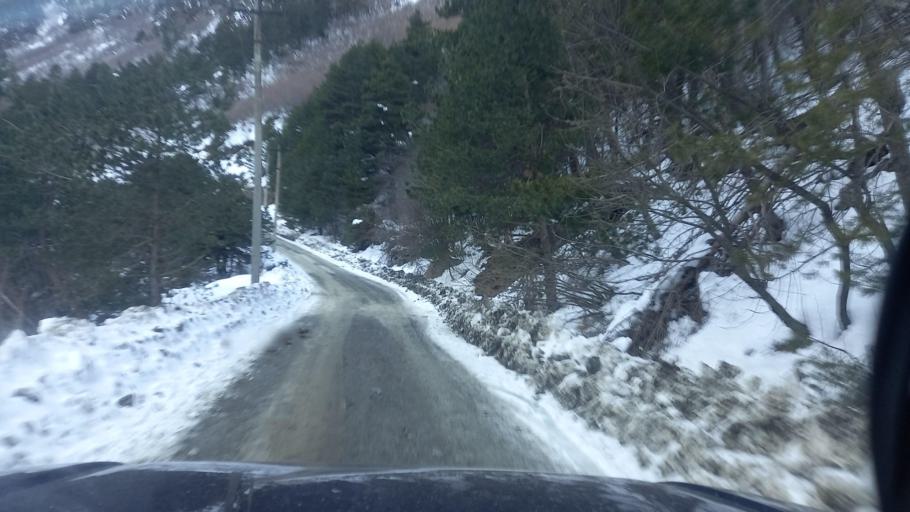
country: RU
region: Kabardino-Balkariya
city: Verkhnyaya Balkariya
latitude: 42.9024
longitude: 43.5953
